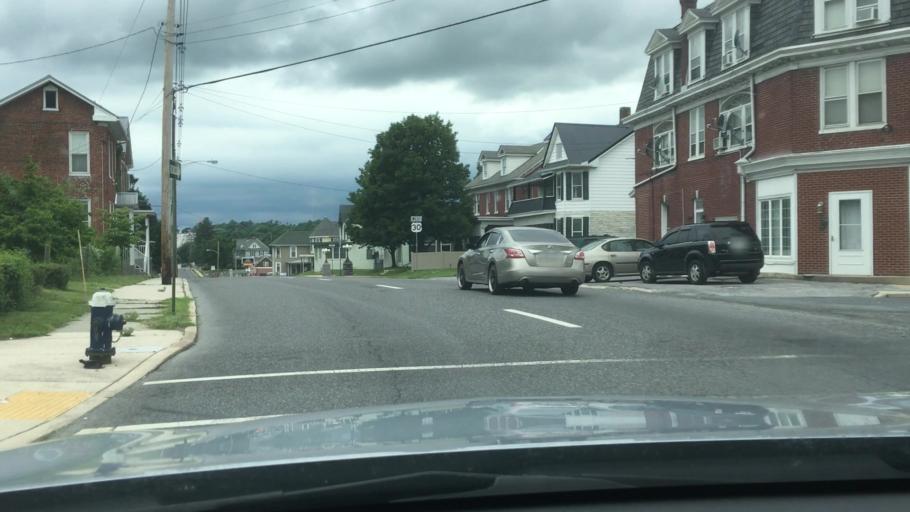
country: US
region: Pennsylvania
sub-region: Franklin County
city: Chambersburg
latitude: 39.9385
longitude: -77.6693
